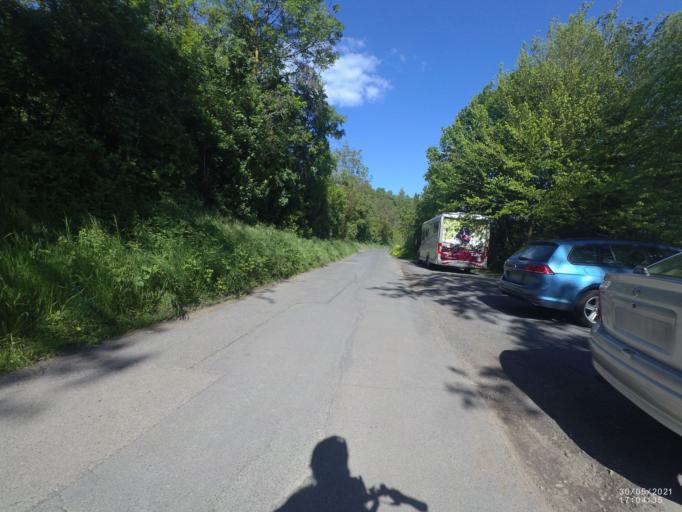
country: DE
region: Rheinland-Pfalz
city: Rhens
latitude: 50.2819
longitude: 7.6063
